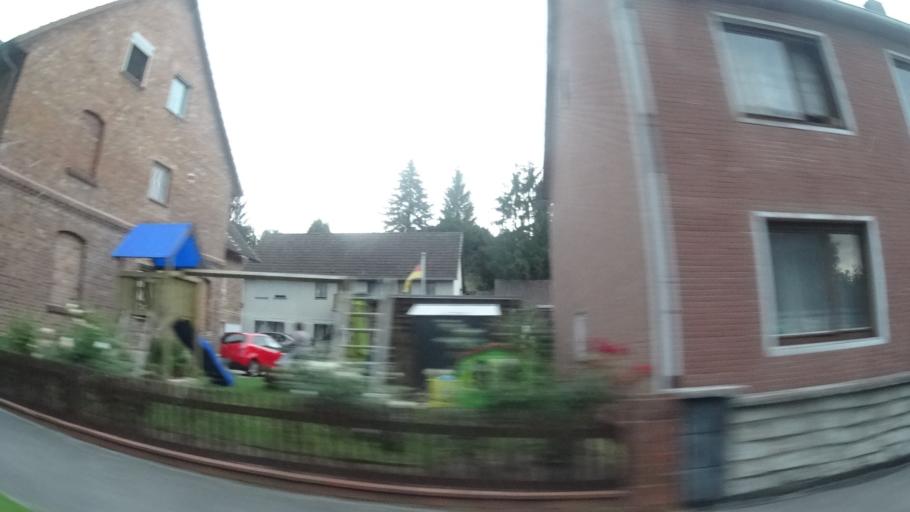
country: DE
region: Lower Saxony
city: Halle
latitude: 51.9927
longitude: 9.5598
